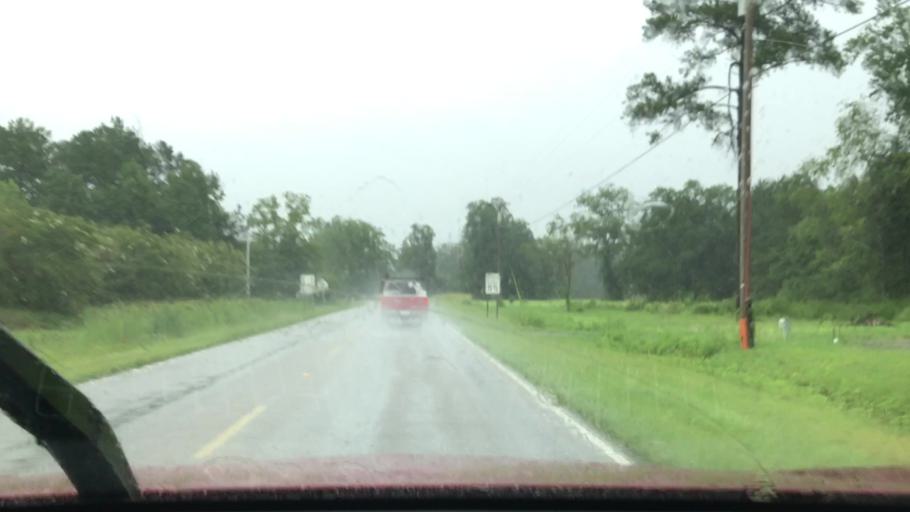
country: US
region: South Carolina
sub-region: Horry County
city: Red Hill
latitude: 33.8577
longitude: -79.0018
